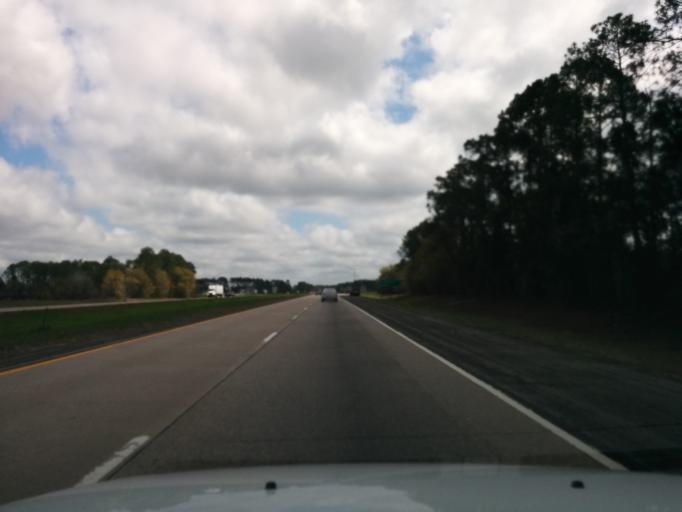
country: US
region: Georgia
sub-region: Chatham County
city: Bloomingdale
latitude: 32.1727
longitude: -81.4492
